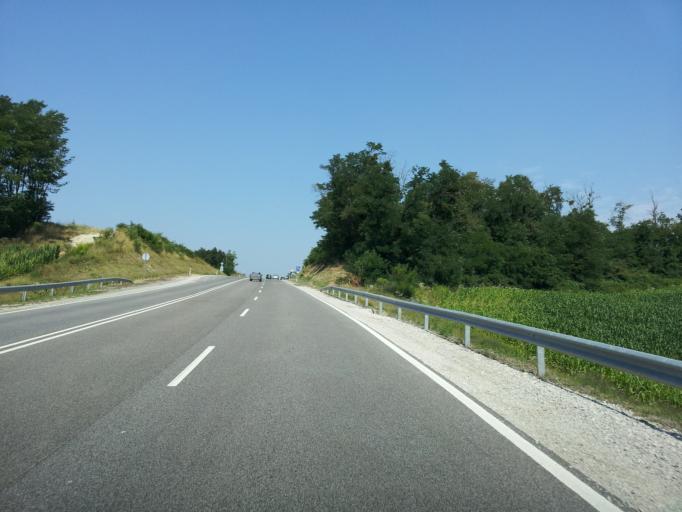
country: HU
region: Zala
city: Pacsa
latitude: 46.8292
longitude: 17.0515
